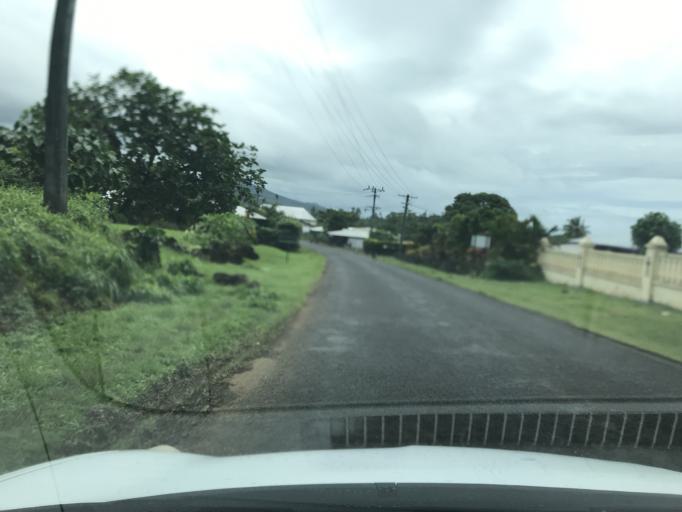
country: WS
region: Atua
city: Lufilufi
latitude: -13.8757
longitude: -171.6002
